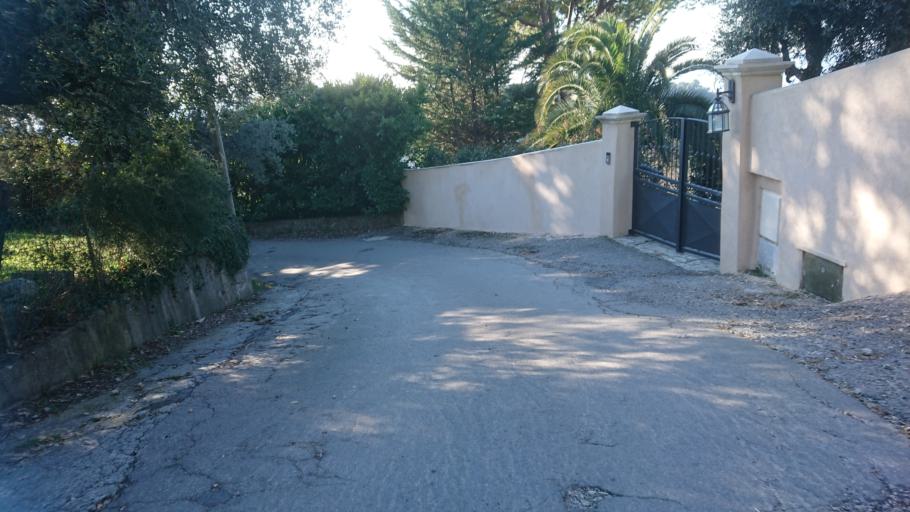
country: FR
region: Provence-Alpes-Cote d'Azur
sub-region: Departement des Alpes-Maritimes
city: Opio
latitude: 43.6840
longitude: 6.9705
